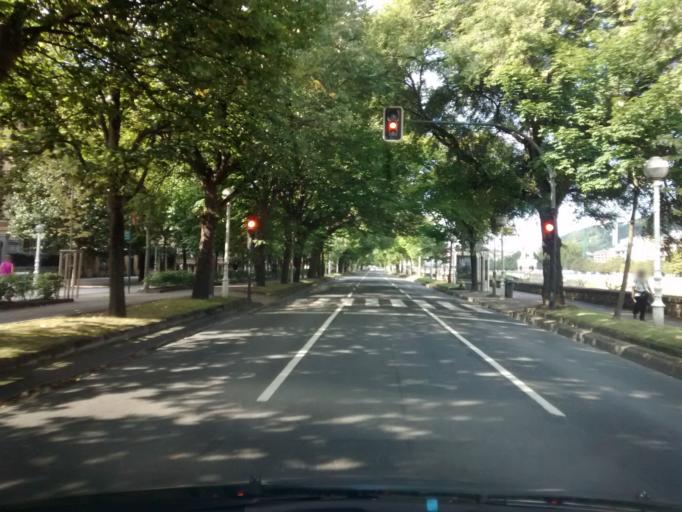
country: ES
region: Basque Country
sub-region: Provincia de Guipuzcoa
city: San Sebastian
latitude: 43.3136
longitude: -1.9794
